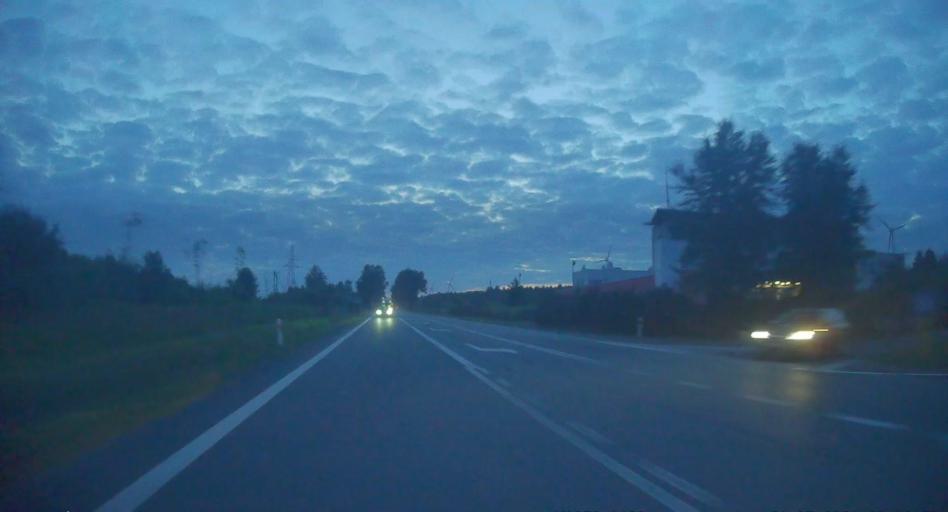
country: PL
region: Silesian Voivodeship
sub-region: Powiat klobucki
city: Klobuck
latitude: 50.9070
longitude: 18.9182
